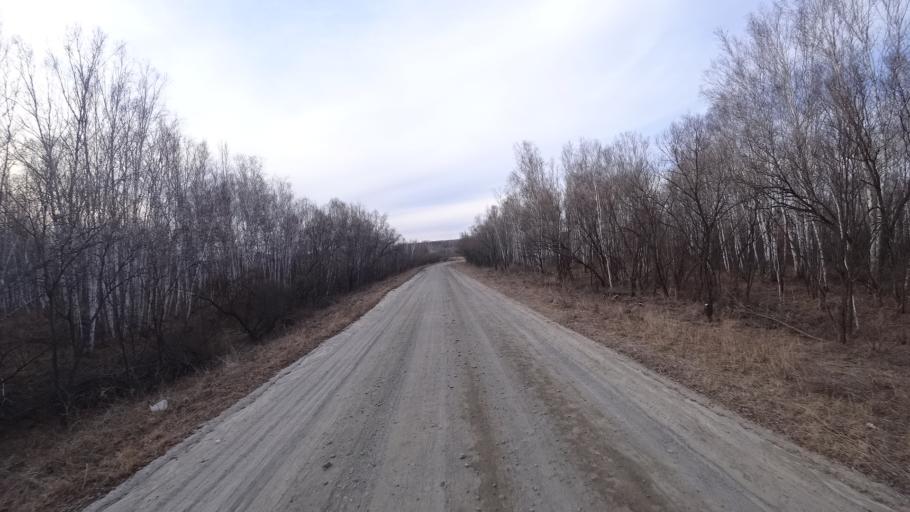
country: RU
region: Amur
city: Bureya
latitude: 50.0157
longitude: 129.7741
